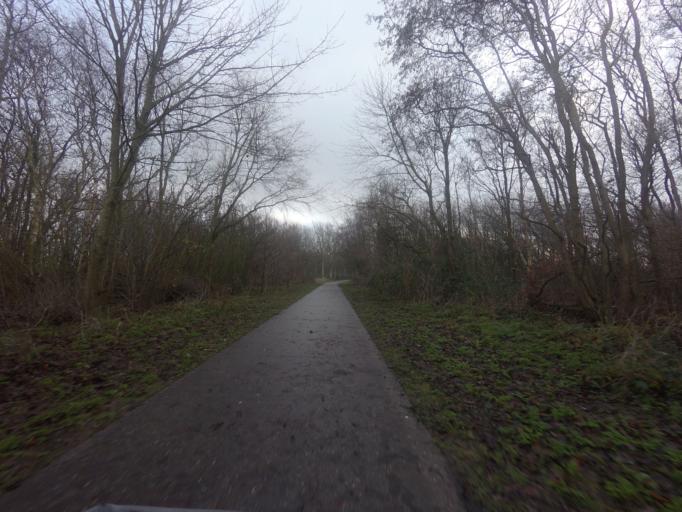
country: NL
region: North Holland
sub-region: Gemeente Texel
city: Den Burg
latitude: 53.1637
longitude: 4.8515
